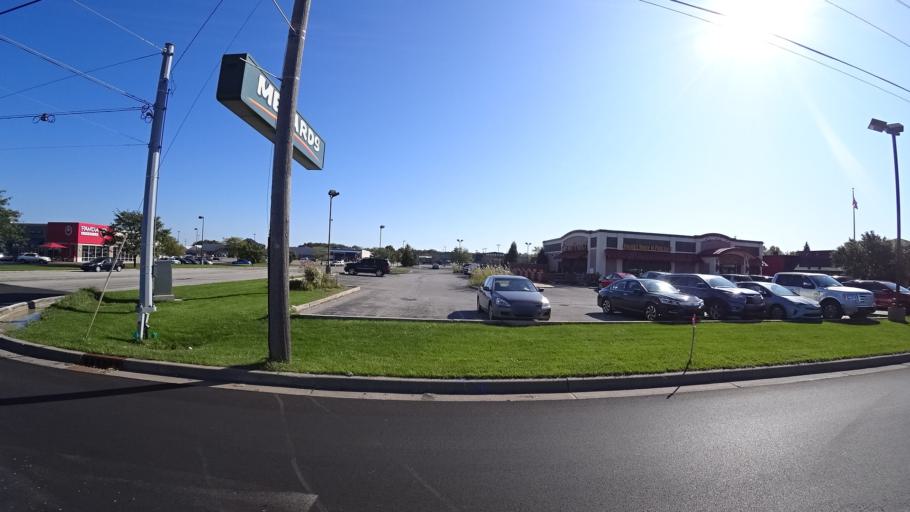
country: US
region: Indiana
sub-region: LaPorte County
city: Michigan City
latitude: 41.6714
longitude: -86.8939
